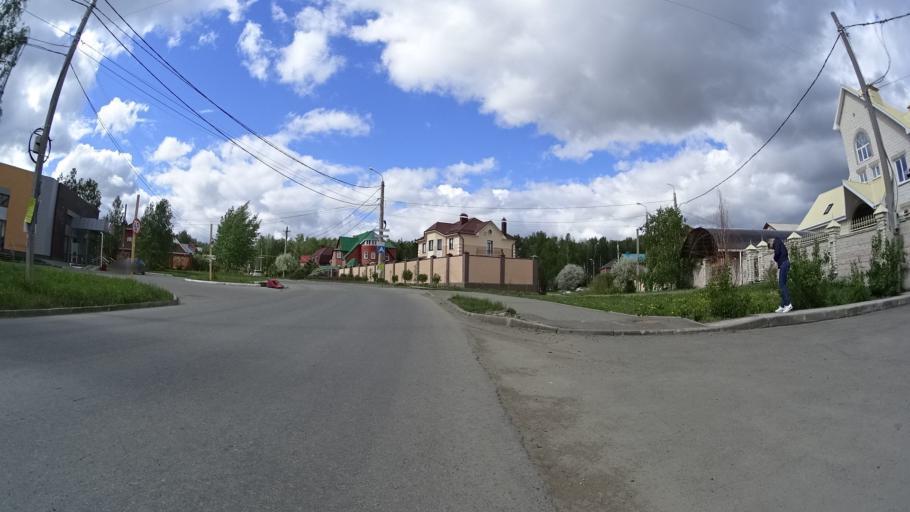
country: RU
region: Chelyabinsk
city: Sargazy
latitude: 55.1540
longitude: 61.2547
